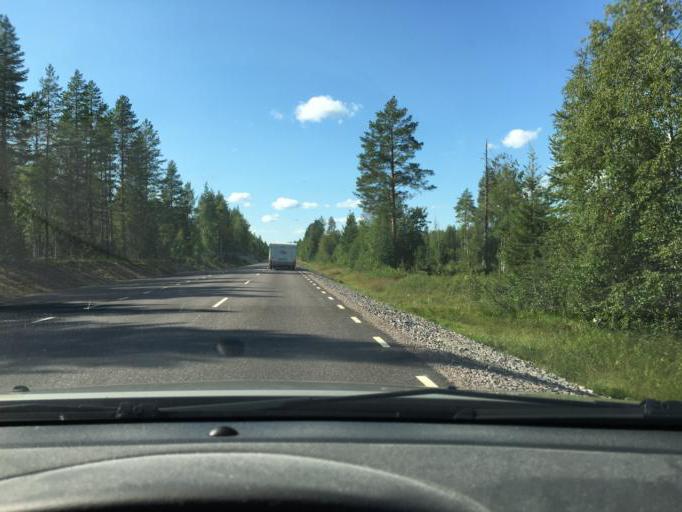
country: SE
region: Norrbotten
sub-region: Lulea Kommun
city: Ranea
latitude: 66.0497
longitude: 22.2308
